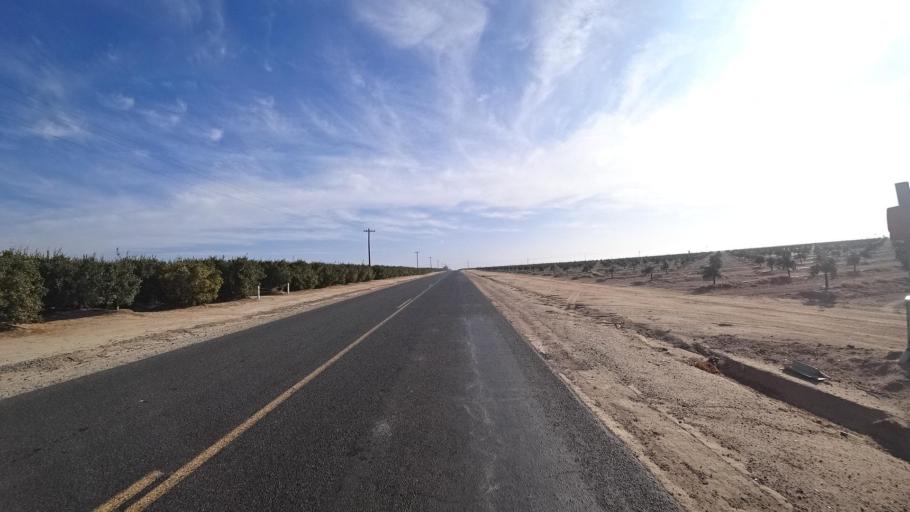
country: US
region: California
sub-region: Kern County
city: McFarland
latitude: 35.6021
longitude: -119.1213
